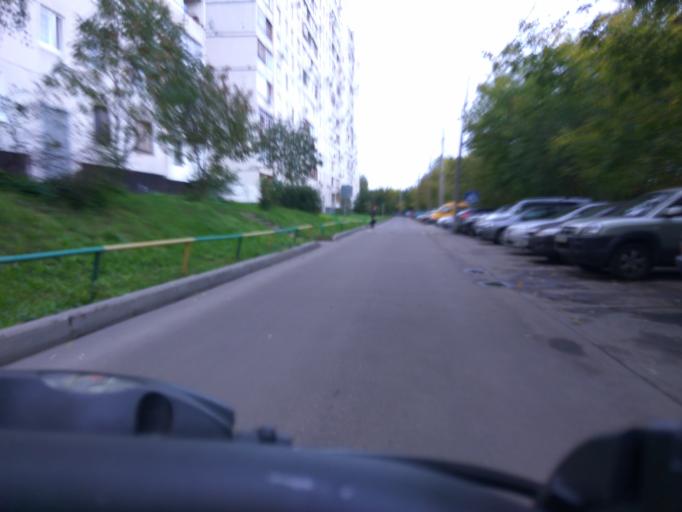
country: RU
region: Moscow
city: Kozeyevo
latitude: 55.8749
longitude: 37.6185
